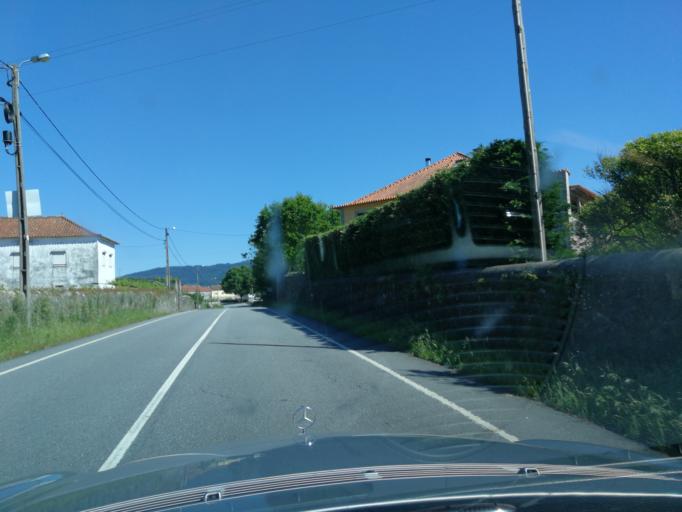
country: PT
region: Viana do Castelo
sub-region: Viana do Castelo
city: Darque
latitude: 41.7108
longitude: -8.7495
